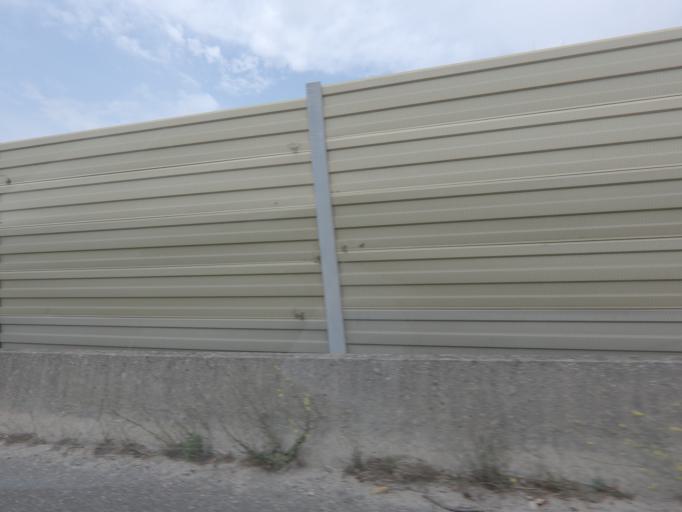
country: PT
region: Aveiro
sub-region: Mealhada
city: Pampilhosa do Botao
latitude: 40.2903
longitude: -8.4302
